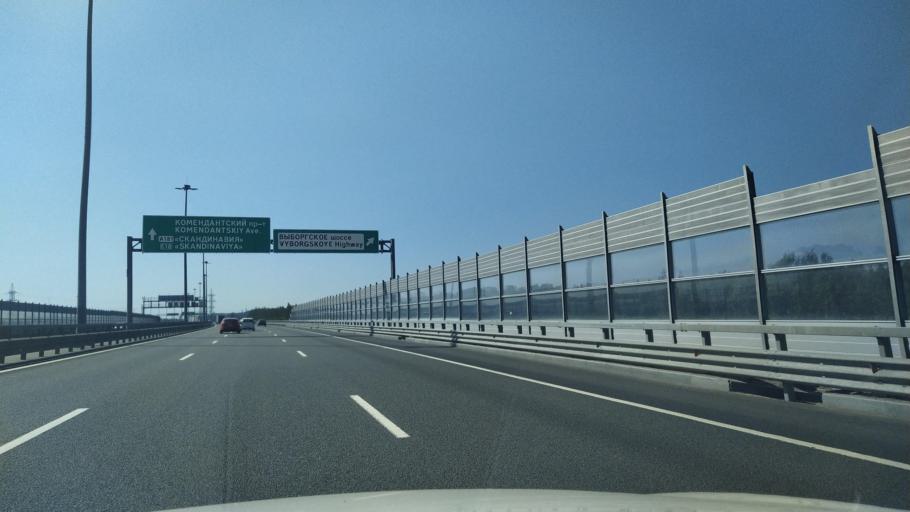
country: RU
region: St.-Petersburg
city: Pargolovo
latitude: 60.0982
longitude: 30.2946
